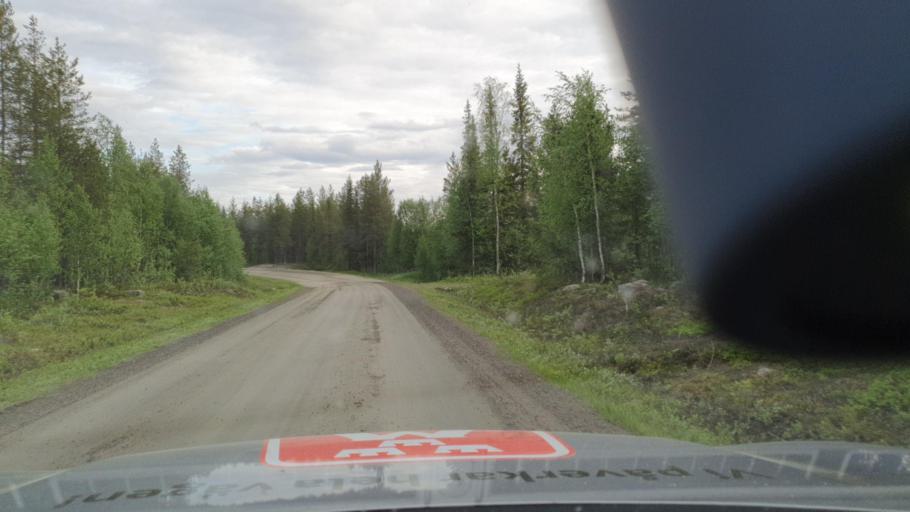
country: SE
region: Norrbotten
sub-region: Gallivare Kommun
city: Gaellivare
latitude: 66.6952
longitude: 21.1630
